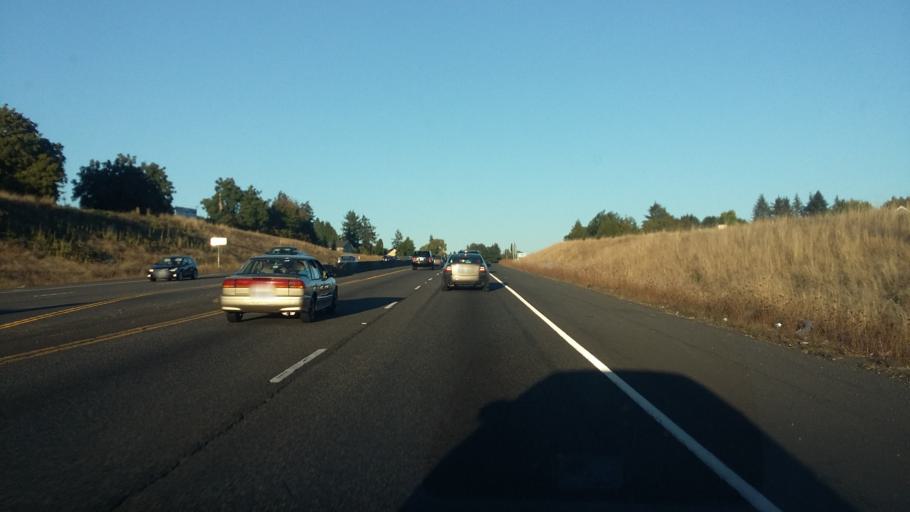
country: US
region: Washington
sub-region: Clark County
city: Minnehaha
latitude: 45.6472
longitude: -122.6273
